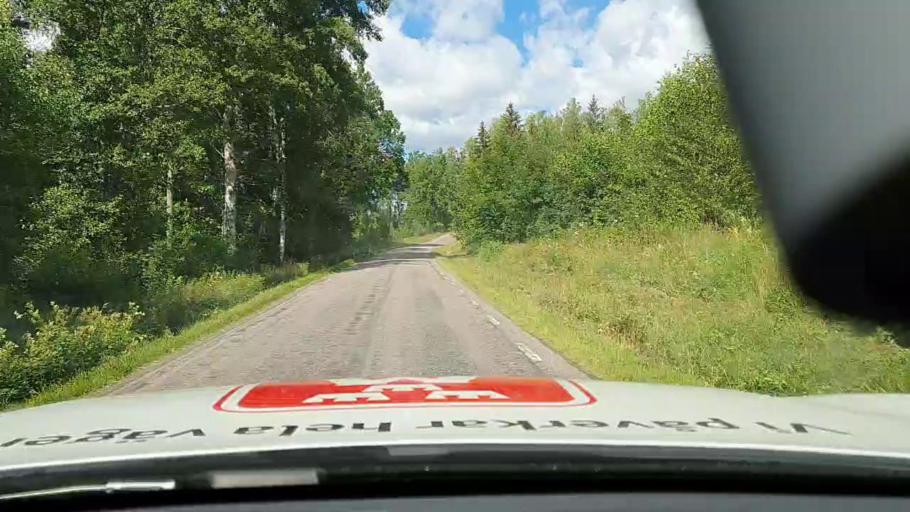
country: SE
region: Vaestra Goetaland
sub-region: Karlsborgs Kommun
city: Molltorp
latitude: 58.5962
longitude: 14.2638
